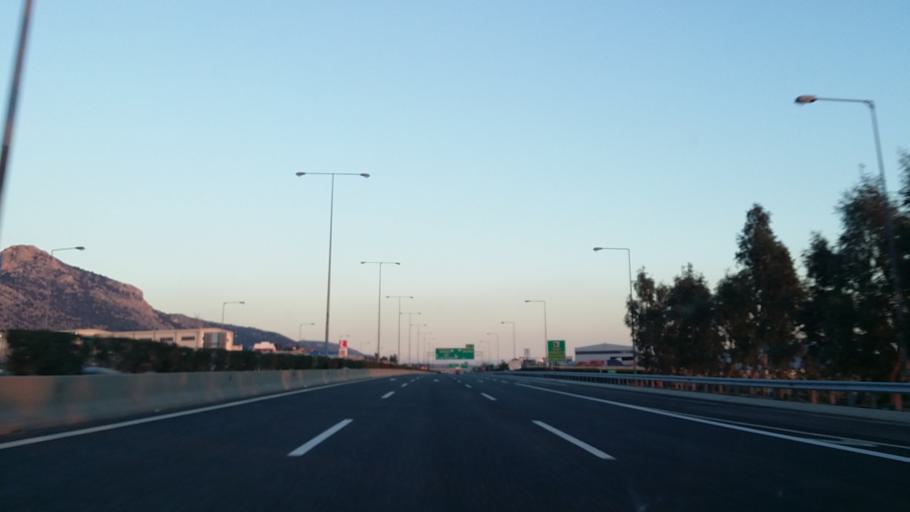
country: GR
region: Attica
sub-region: Nomarchia Dytikis Attikis
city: Aspropyrgos
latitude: 38.0925
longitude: 23.6077
